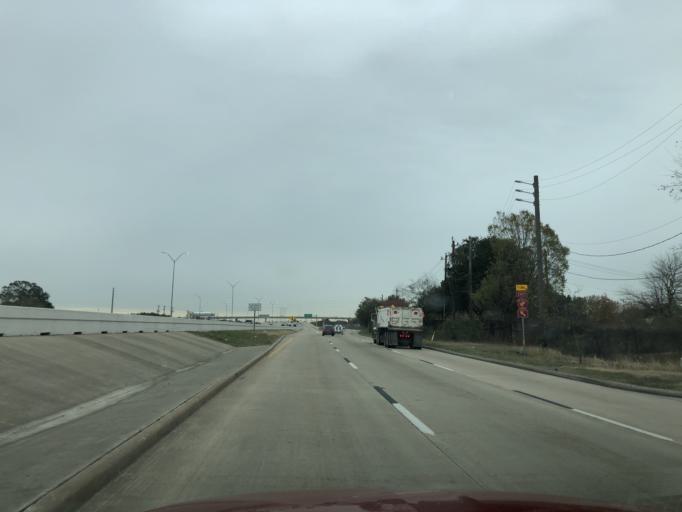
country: US
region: Texas
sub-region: Fort Bend County
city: Missouri City
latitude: 29.6172
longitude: -95.5012
